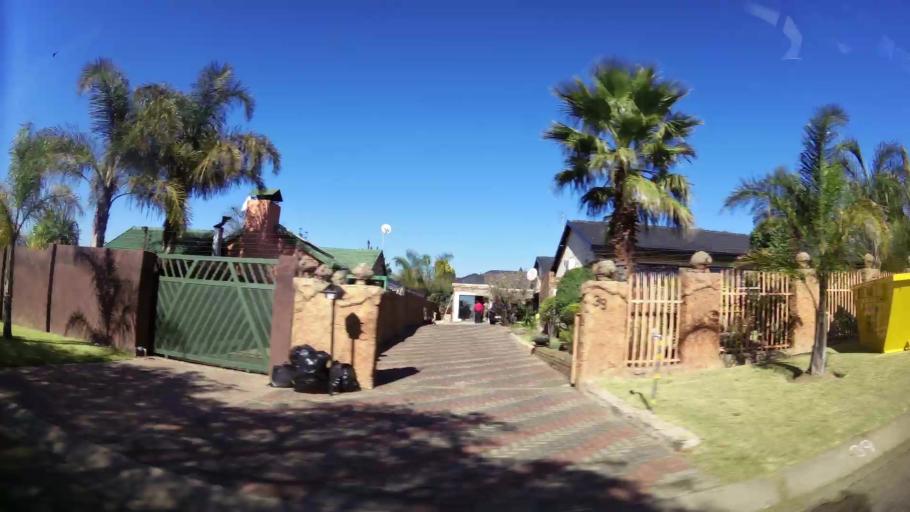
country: ZA
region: Mpumalanga
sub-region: Nkangala District Municipality
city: Witbank
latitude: -25.8704
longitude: 29.2440
